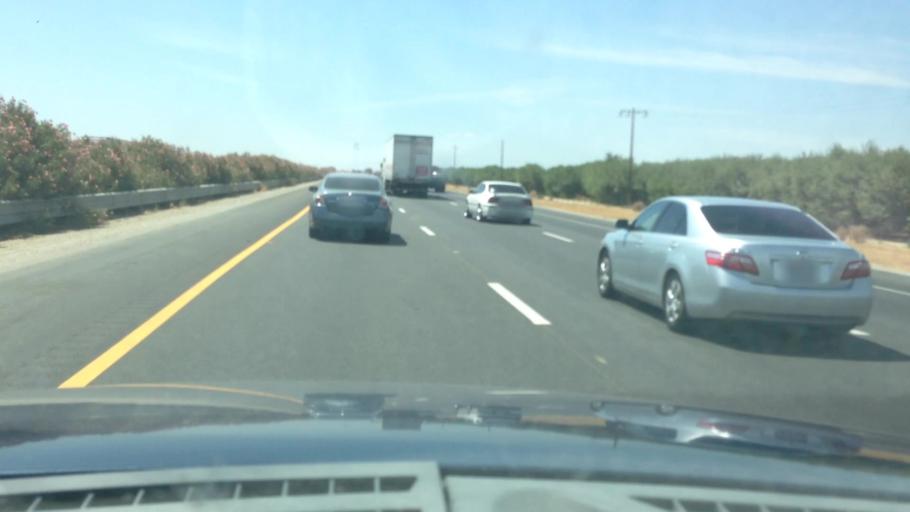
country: US
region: California
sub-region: Kern County
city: McFarland
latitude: 35.6275
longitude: -119.2155
